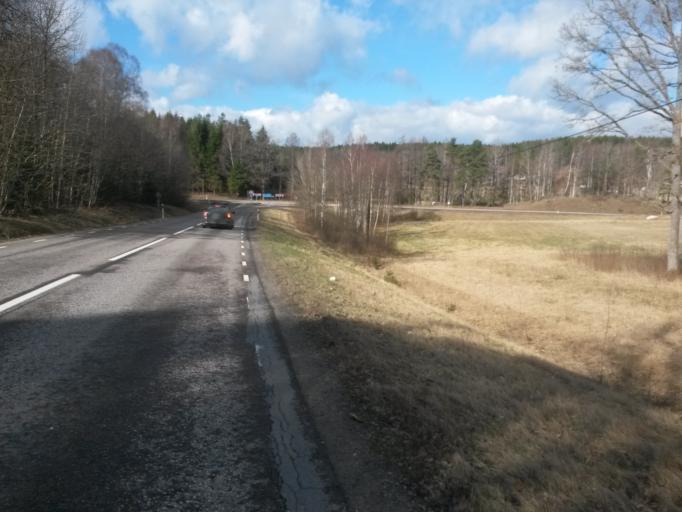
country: SE
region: Vaestra Goetaland
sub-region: Vargarda Kommun
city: Jonstorp
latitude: 58.0631
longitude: 12.6826
